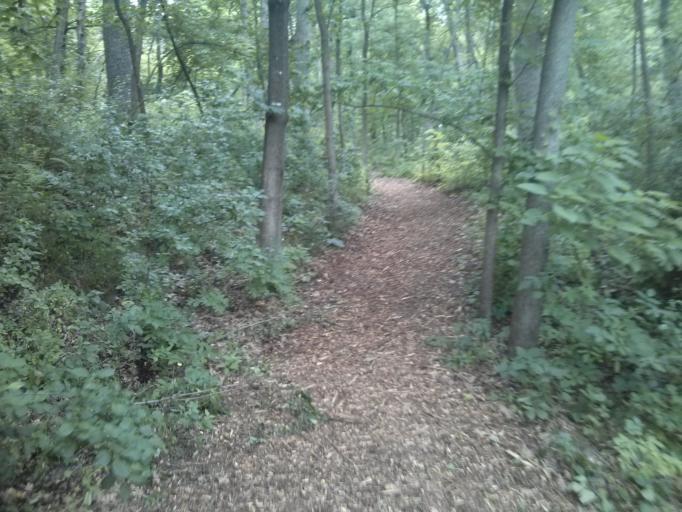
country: US
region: Wisconsin
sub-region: Saint Croix County
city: Hudson
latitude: 44.9737
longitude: -92.7551
